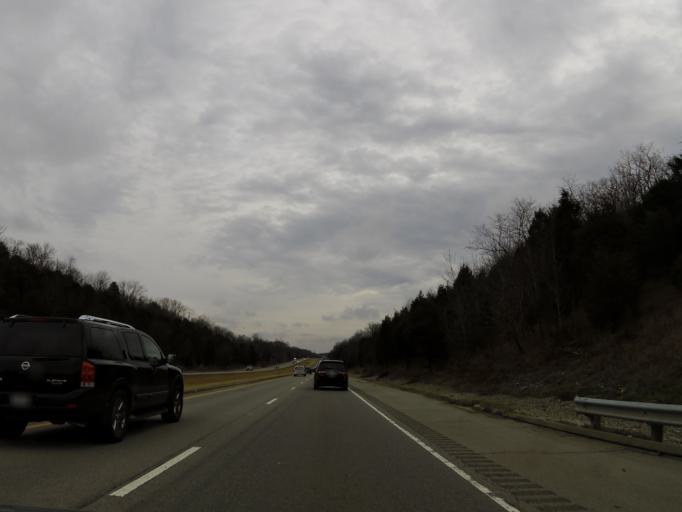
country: US
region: Indiana
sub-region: Dearborn County
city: Bright
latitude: 39.2732
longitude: -84.9294
